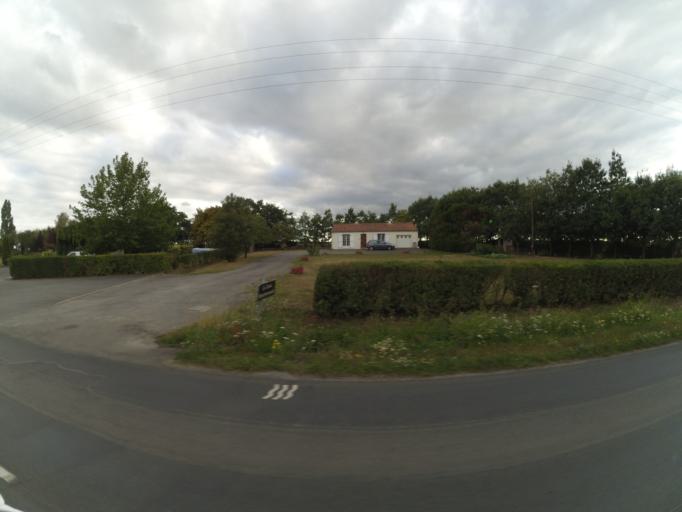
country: FR
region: Pays de la Loire
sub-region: Departement de la Vendee
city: Saint-Andre-Treize-Voies
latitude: 46.9189
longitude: -1.3894
